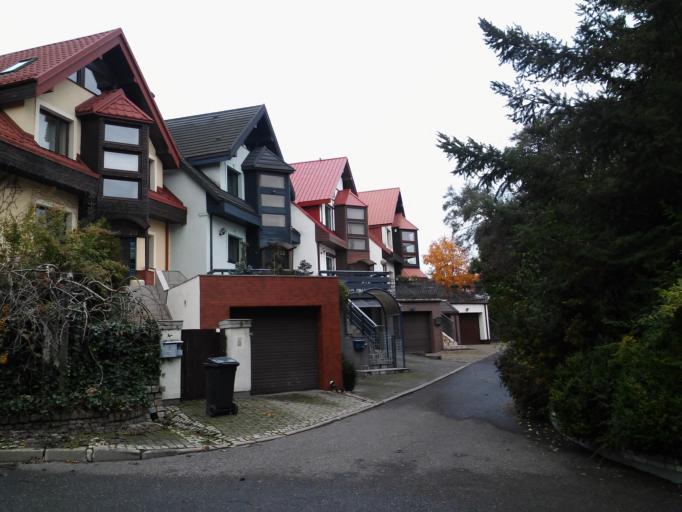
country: PL
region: Pomeranian Voivodeship
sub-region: Gdansk
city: Gdansk
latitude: 54.3767
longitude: 18.5911
